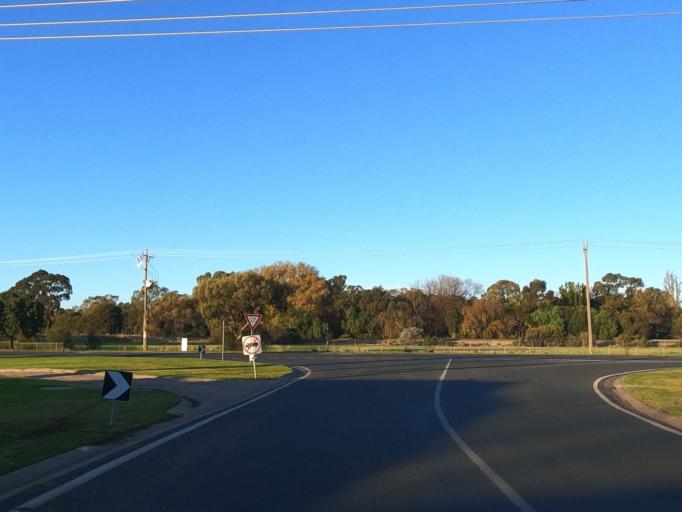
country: AU
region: Victoria
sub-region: Swan Hill
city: Swan Hill
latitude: -35.3587
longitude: 143.5618
